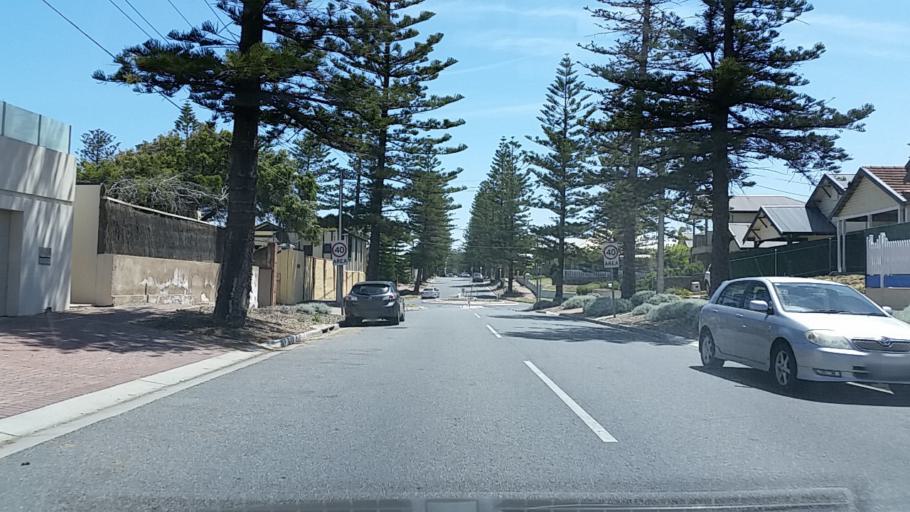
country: AU
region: South Australia
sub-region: Charles Sturt
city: Grange
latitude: -34.9059
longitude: 138.4907
